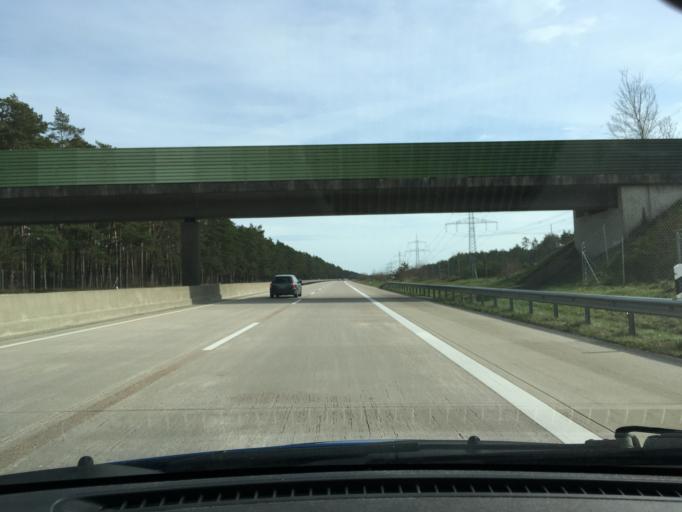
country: DE
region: Schleswig-Holstein
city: Gudow
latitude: 53.5302
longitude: 10.7652
